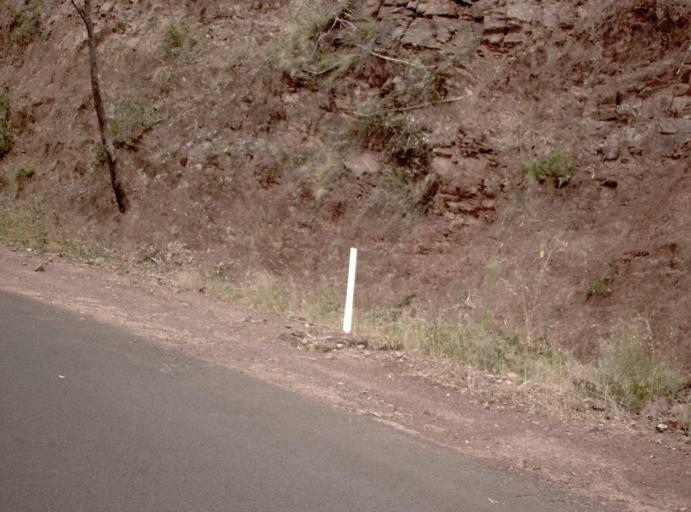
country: AU
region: Victoria
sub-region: Wellington
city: Heyfield
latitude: -37.7060
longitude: 146.6664
